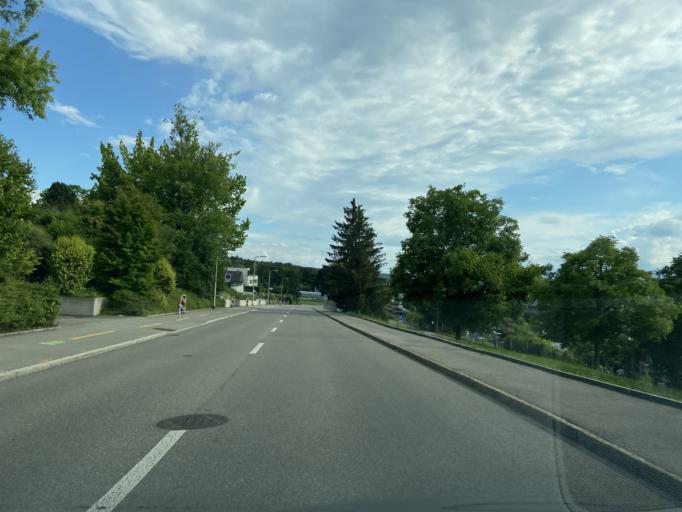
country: CH
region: Zurich
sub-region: Bezirk Winterthur
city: Veltheim
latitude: 47.5220
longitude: 8.7216
